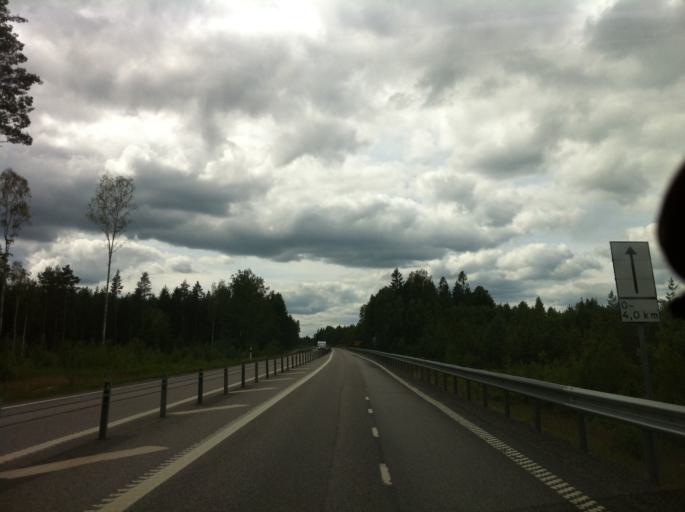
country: SE
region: Kalmar
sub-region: Nybro Kommun
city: Nybro
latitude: 56.7229
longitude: 15.8017
